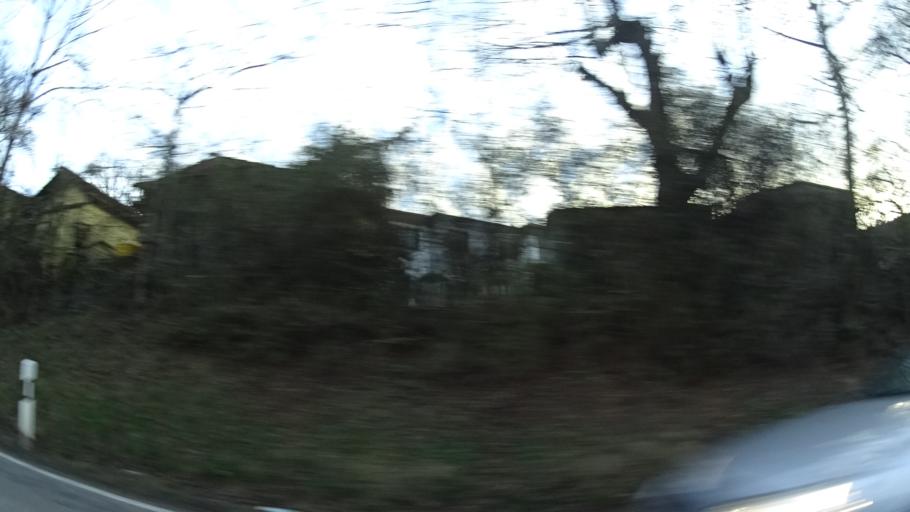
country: DE
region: Baden-Wuerttemberg
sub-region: Regierungsbezirk Stuttgart
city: Hemmingen
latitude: 48.8826
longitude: 9.0086
